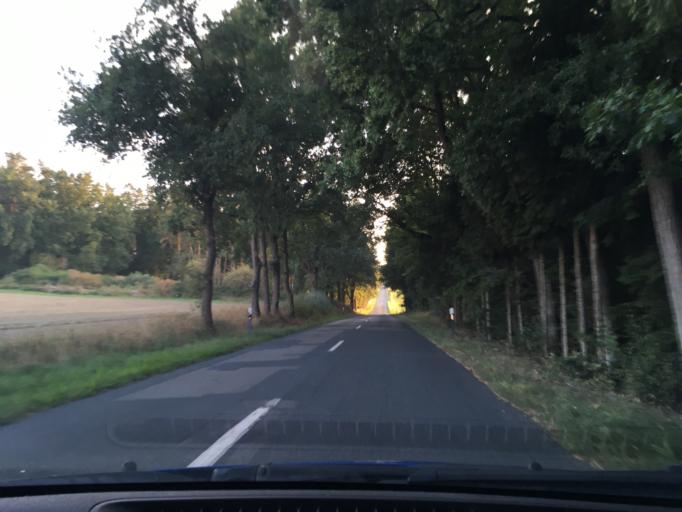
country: DE
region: Lower Saxony
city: Tosterglope
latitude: 53.2493
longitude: 10.7940
